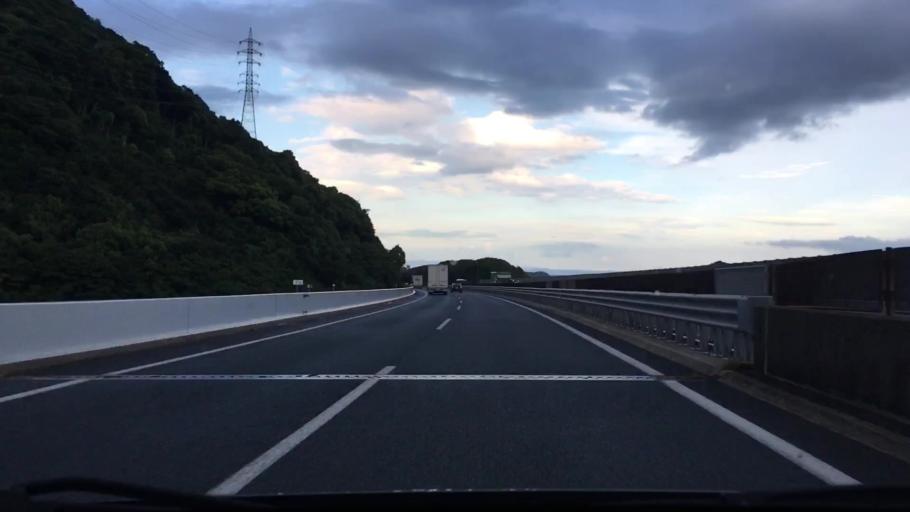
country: JP
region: Yamaguchi
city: Shimonoseki
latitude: 33.8661
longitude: 130.9523
